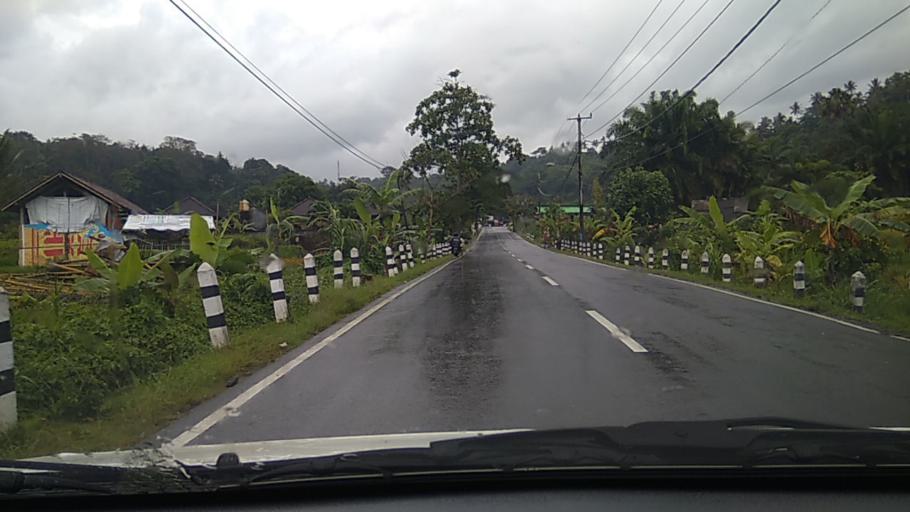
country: ID
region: Bali
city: Banjar Ababi
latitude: -8.4143
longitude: 115.5891
